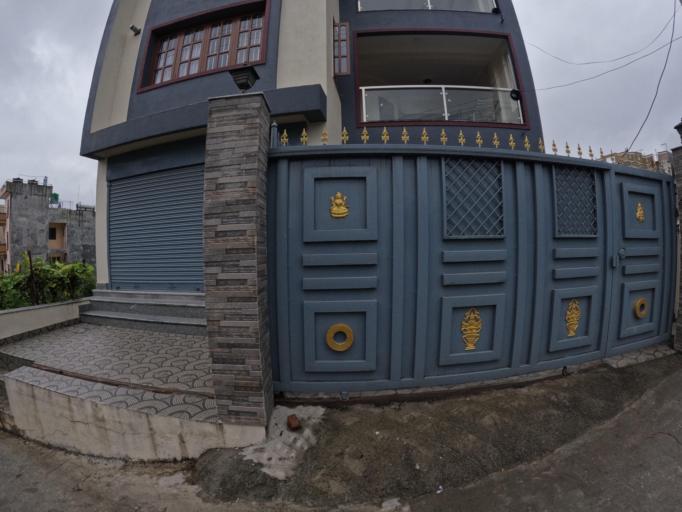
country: NP
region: Central Region
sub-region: Bagmati Zone
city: Kathmandu
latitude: 27.7648
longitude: 85.3189
